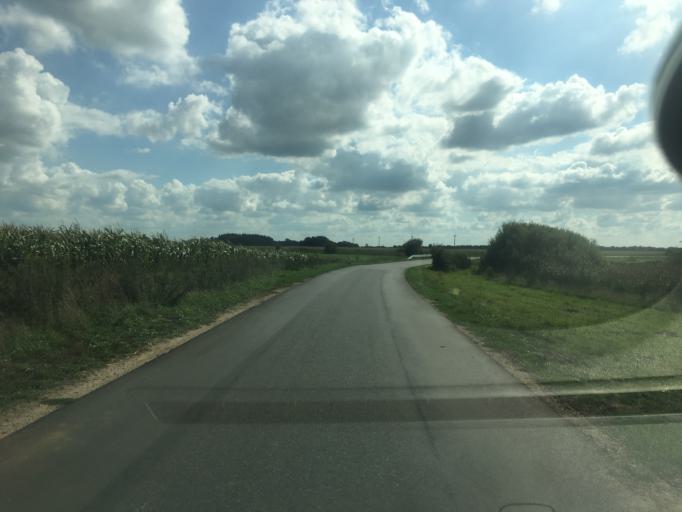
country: DK
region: South Denmark
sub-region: Tonder Kommune
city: Logumkloster
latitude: 54.9947
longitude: 9.0112
